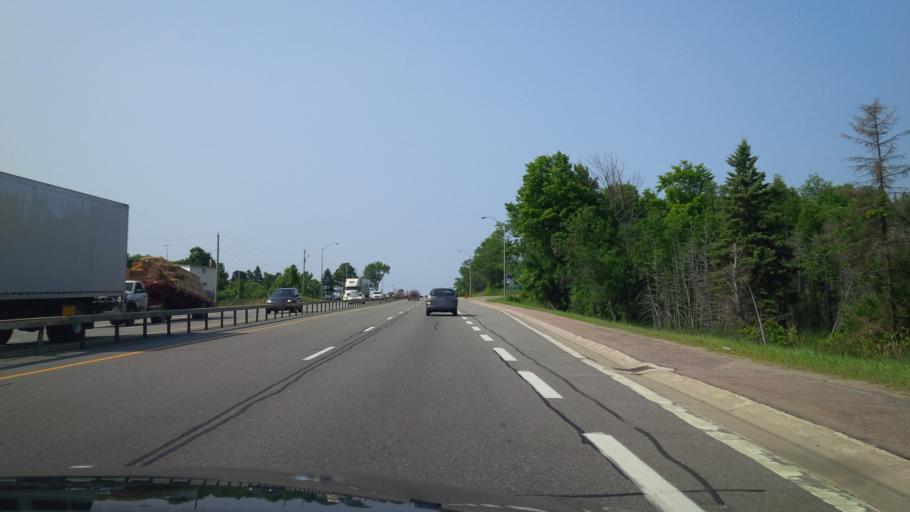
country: CA
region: Ontario
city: Orillia
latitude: 44.5367
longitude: -79.4580
